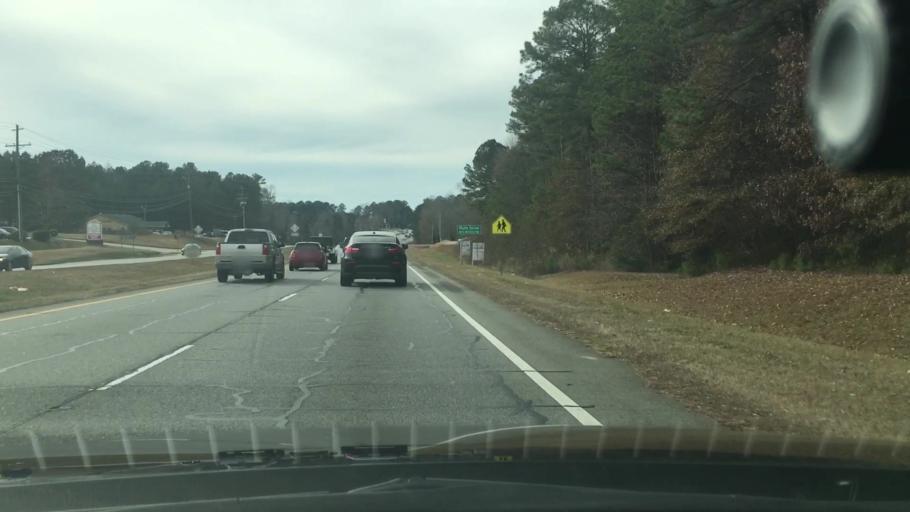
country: US
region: Georgia
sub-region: Coweta County
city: East Newnan
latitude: 33.4065
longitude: -84.6984
